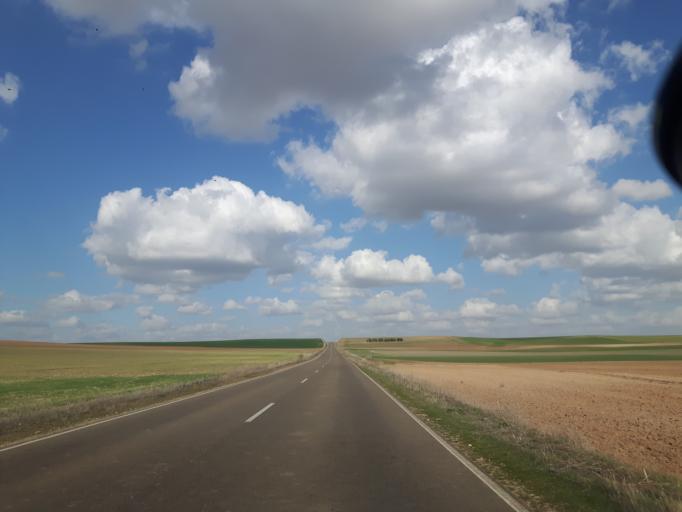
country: ES
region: Castille and Leon
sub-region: Provincia de Salamanca
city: Moriscos
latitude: 40.9959
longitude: -5.5934
